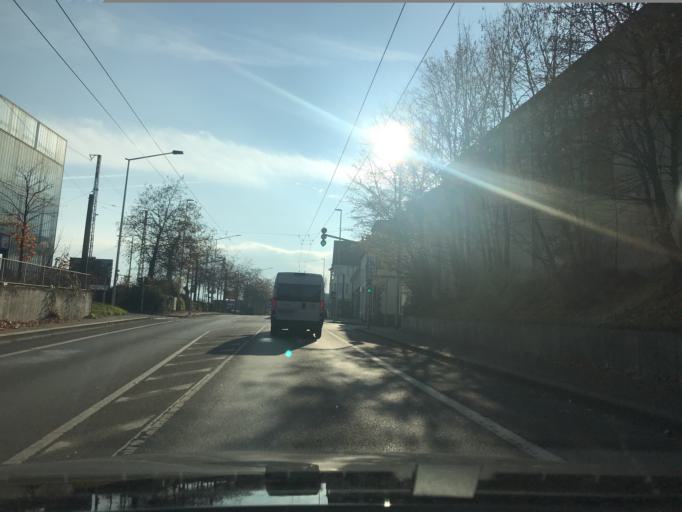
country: DE
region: North Rhine-Westphalia
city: Haan
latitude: 51.1635
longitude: 7.0036
